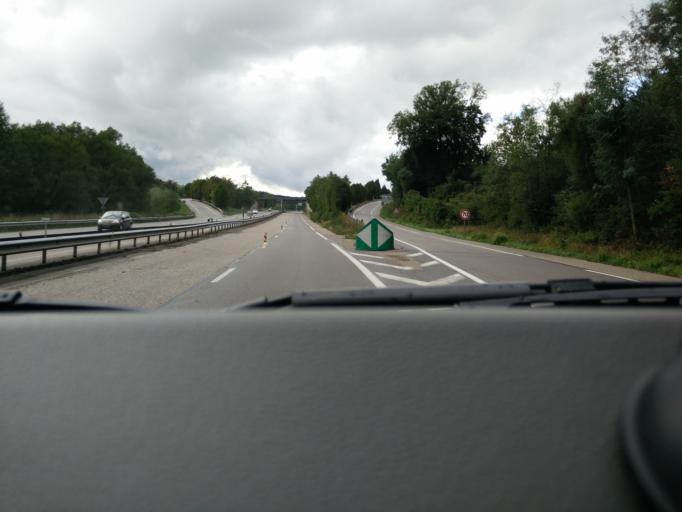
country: FR
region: Lorraine
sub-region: Departement des Vosges
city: Saint-Michel-sur-Meurthe
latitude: 48.3276
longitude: 6.9042
